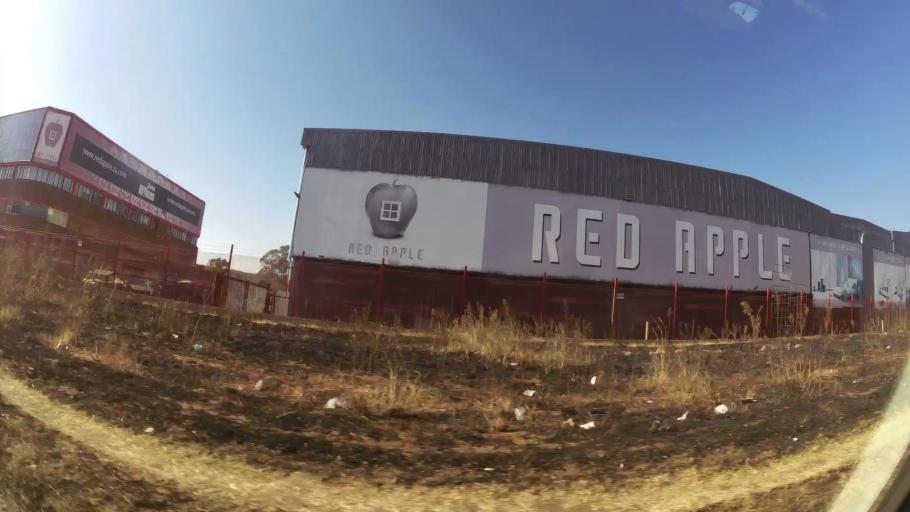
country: ZA
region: Gauteng
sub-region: City of Johannesburg Metropolitan Municipality
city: Johannesburg
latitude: -26.2299
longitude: 28.0903
